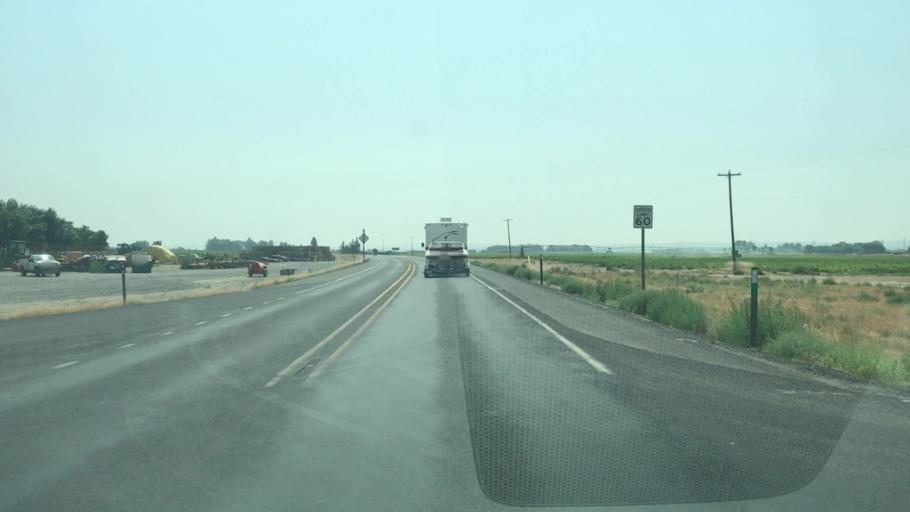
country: US
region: Washington
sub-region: Grant County
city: Quincy
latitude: 47.1177
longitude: -119.8523
